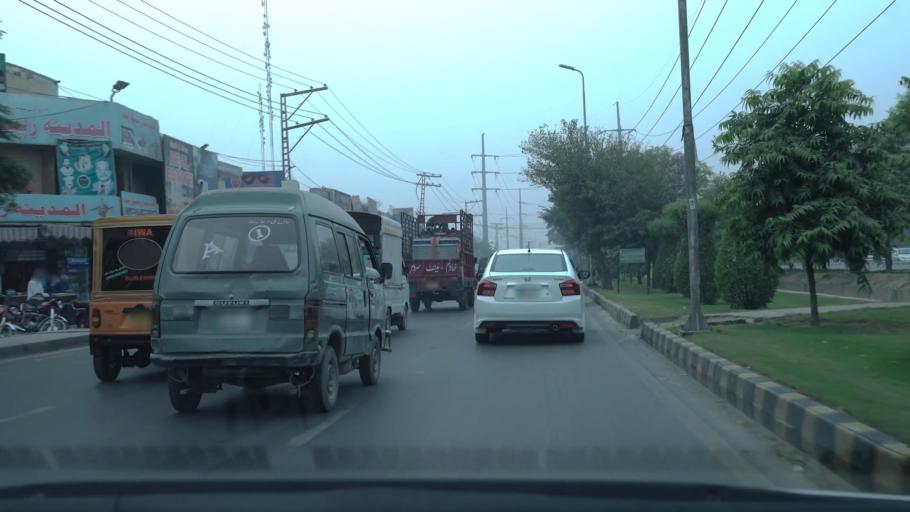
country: PK
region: Punjab
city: Lahore
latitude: 31.4786
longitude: 74.3007
